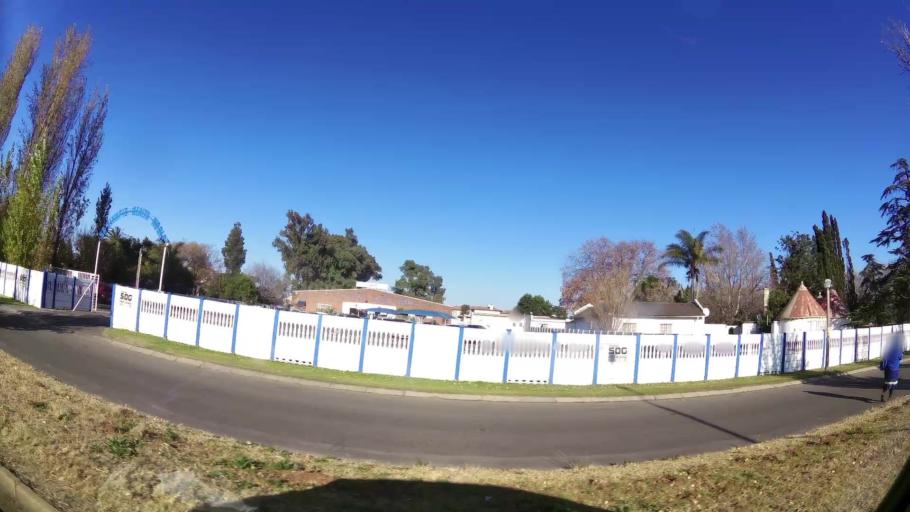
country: ZA
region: Gauteng
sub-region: Ekurhuleni Metropolitan Municipality
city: Germiston
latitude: -26.2836
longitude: 28.1305
